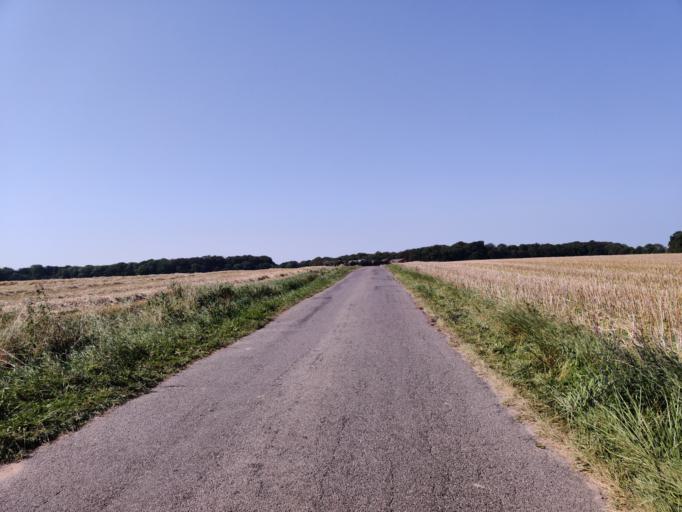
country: DK
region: Zealand
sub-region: Guldborgsund Kommune
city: Nykobing Falster
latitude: 54.6837
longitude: 11.8952
